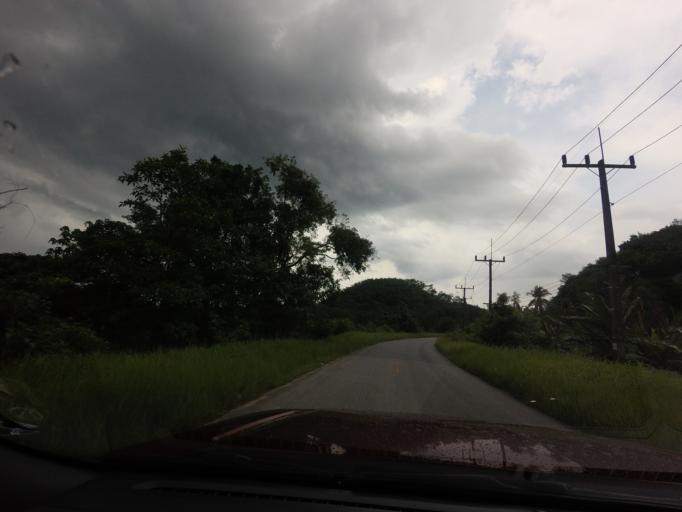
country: TH
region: Yala
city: Ban Nang Sata
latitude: 6.2217
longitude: 101.2290
